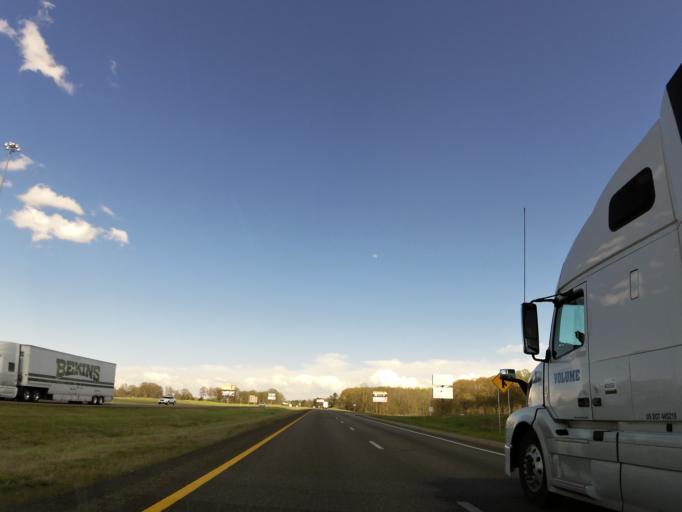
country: US
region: Tennessee
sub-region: Henderson County
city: Lexington
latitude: 35.7893
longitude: -88.3903
